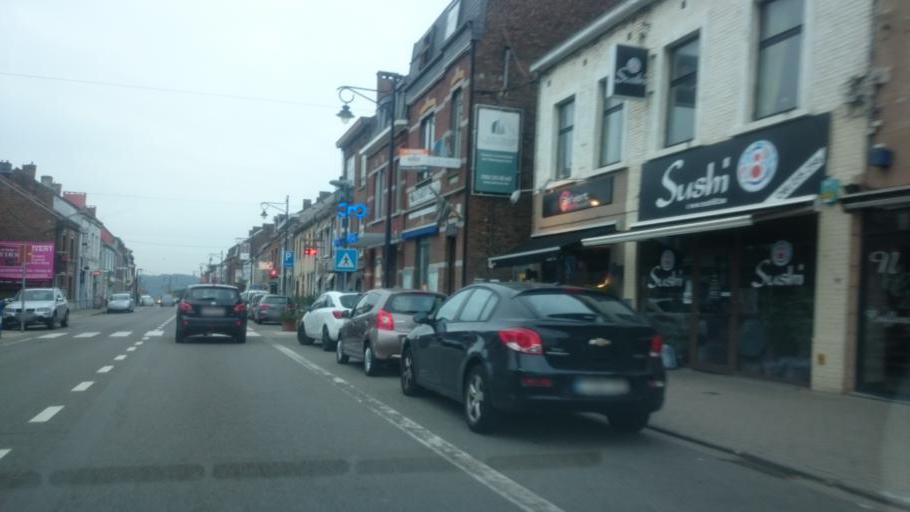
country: BE
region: Wallonia
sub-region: Province de Namur
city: Namur
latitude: 50.4776
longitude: 4.8777
